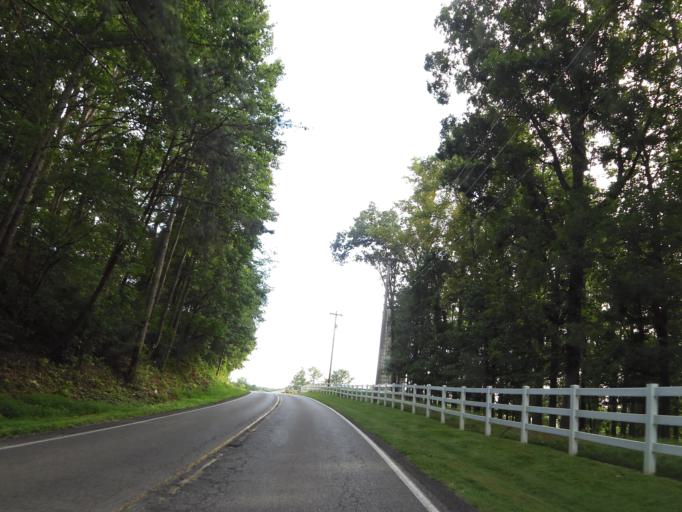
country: US
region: Tennessee
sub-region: Sevier County
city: Seymour
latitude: 35.8631
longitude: -83.8063
